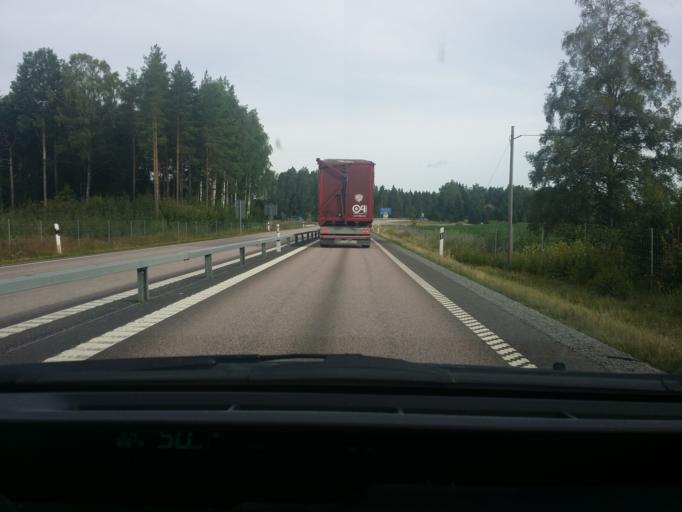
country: SE
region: Vaestmanland
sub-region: Sala Kommun
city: Sala
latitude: 59.8291
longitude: 16.5320
